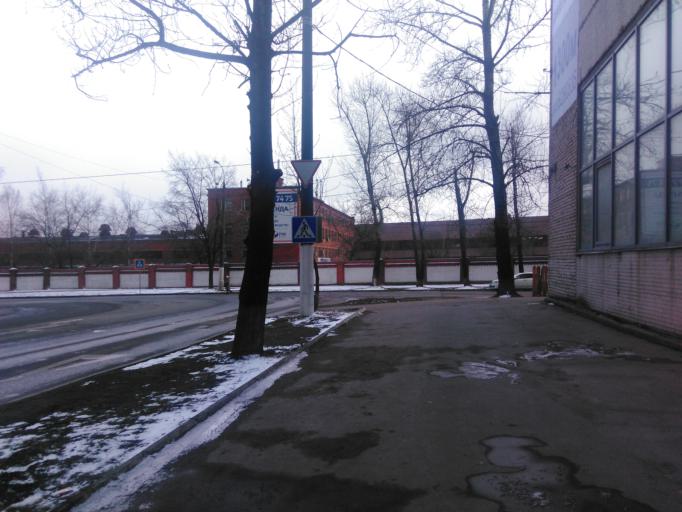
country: RU
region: Moscow
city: Nagornyy
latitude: 55.6434
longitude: 37.6370
